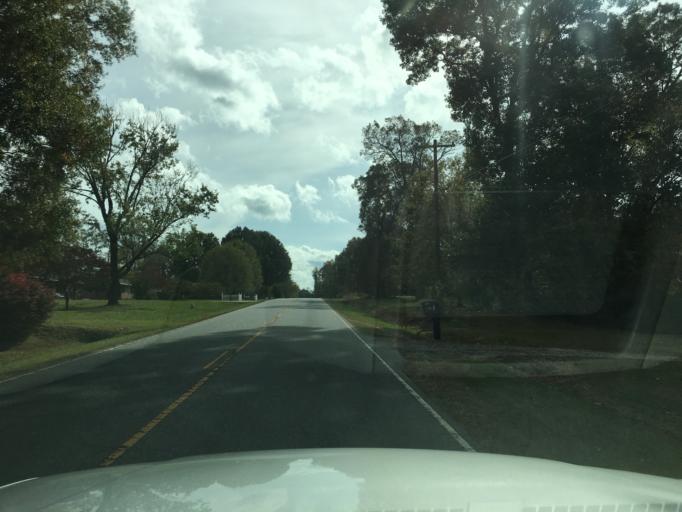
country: US
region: North Carolina
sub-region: Catawba County
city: Newton
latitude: 35.6714
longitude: -81.2731
